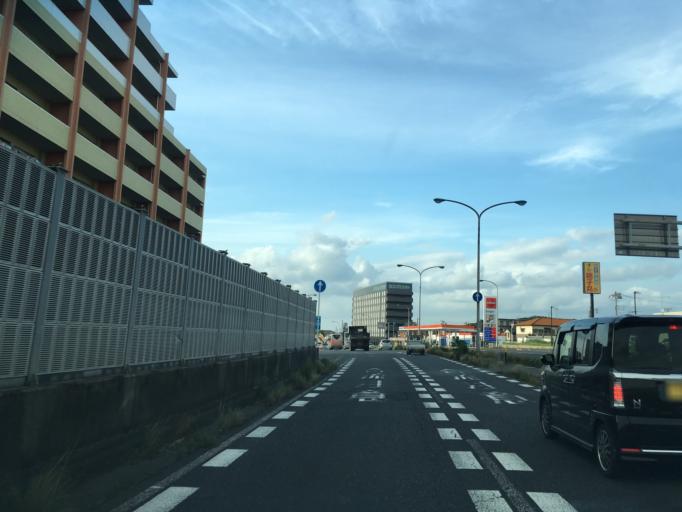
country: JP
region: Chiba
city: Kisarazu
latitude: 35.3794
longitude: 139.9423
